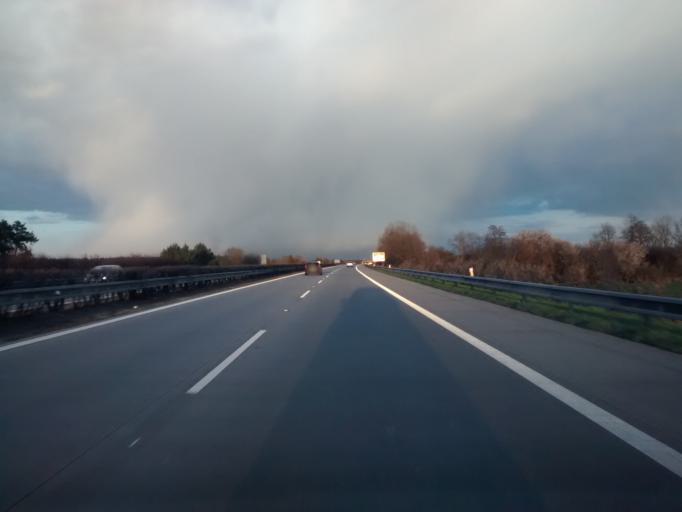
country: CZ
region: Central Bohemia
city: Pecky
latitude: 50.1236
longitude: 15.0340
